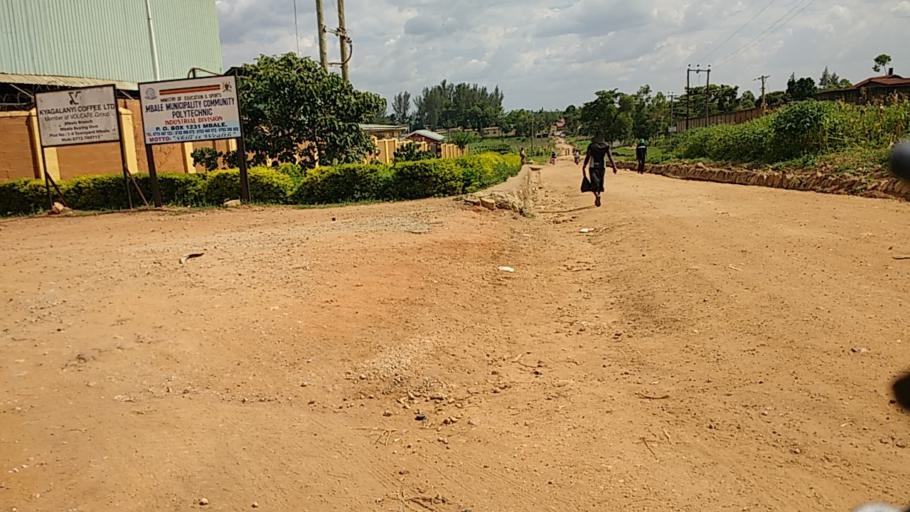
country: UG
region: Eastern Region
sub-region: Mbale District
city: Mbale
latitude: 1.0753
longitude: 34.1594
